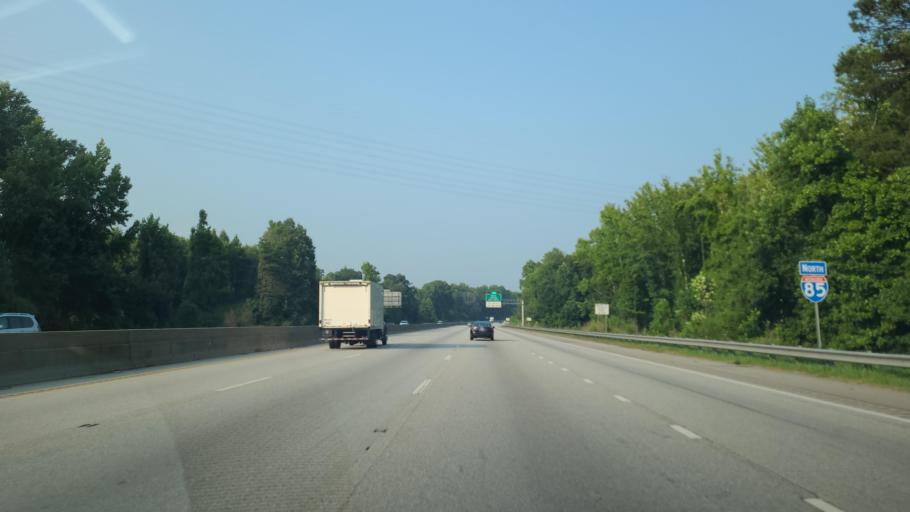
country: US
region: North Carolina
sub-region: Gaston County
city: Bessemer City
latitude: 35.2565
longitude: -81.2902
